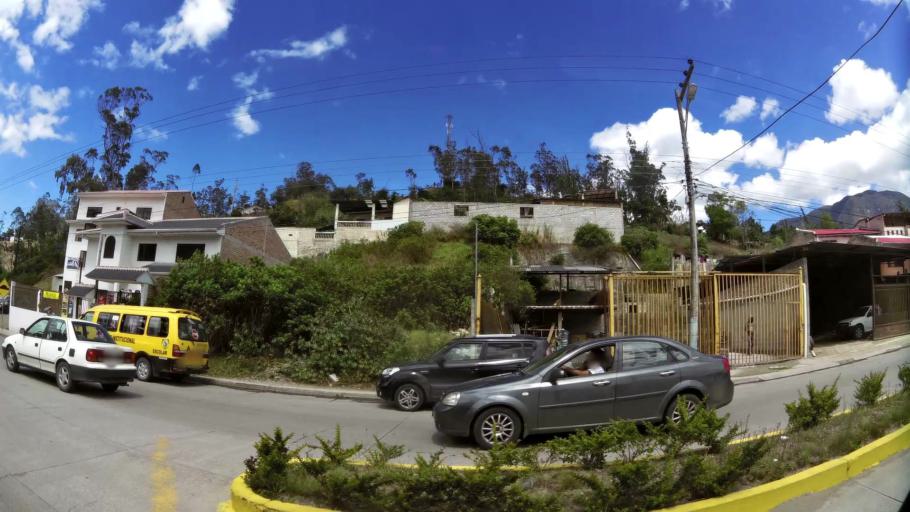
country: EC
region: Azuay
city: Cuenca
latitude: -3.1618
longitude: -79.1515
